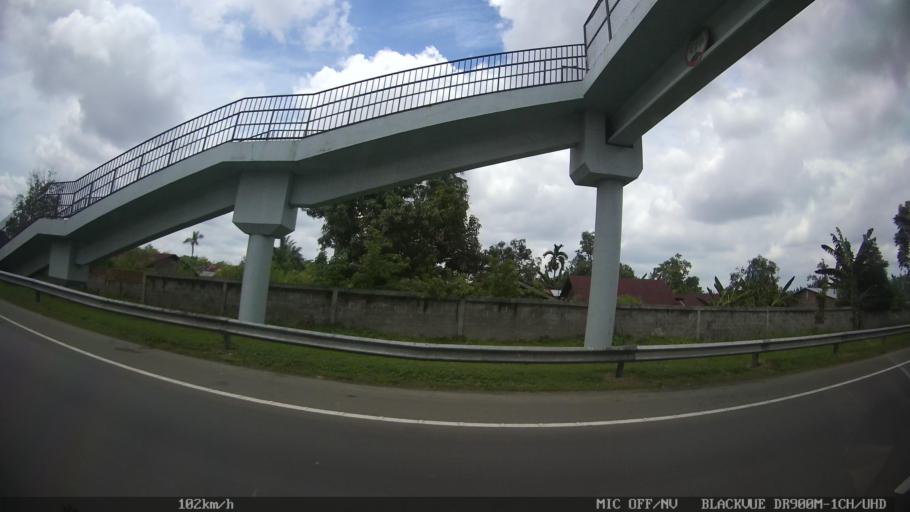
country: ID
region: North Sumatra
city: Medan
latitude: 3.6155
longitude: 98.7211
